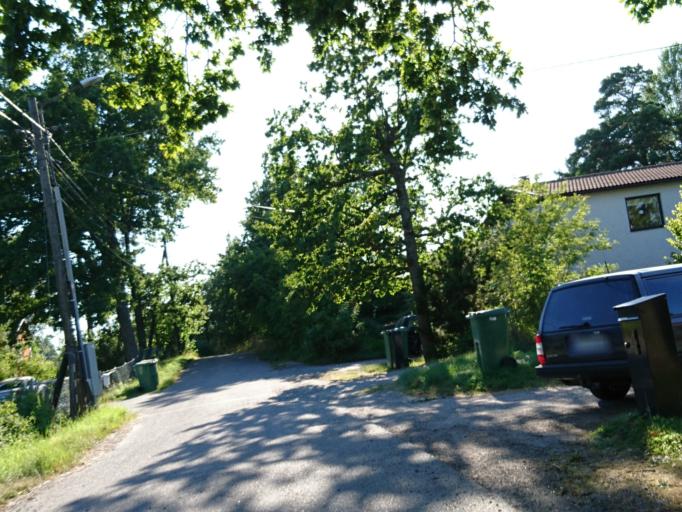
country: SE
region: Stockholm
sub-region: Huddinge Kommun
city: Segeltorp
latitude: 59.2756
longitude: 17.9388
